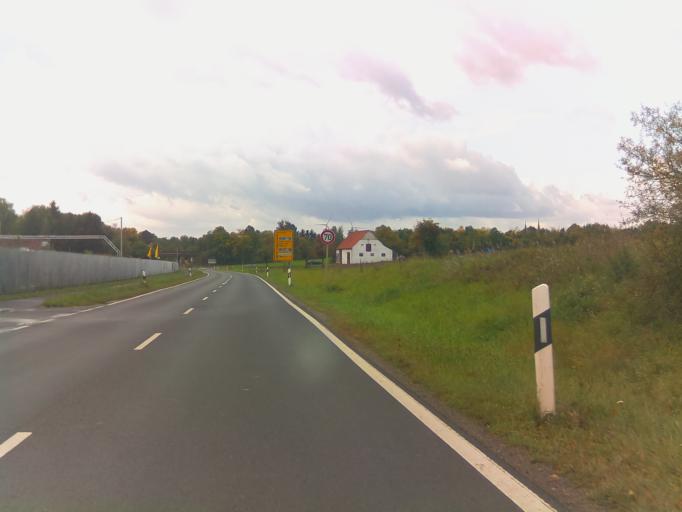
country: DE
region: Bavaria
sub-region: Regierungsbezirk Unterfranken
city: Gerolzhofen
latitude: 49.9016
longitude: 10.3672
